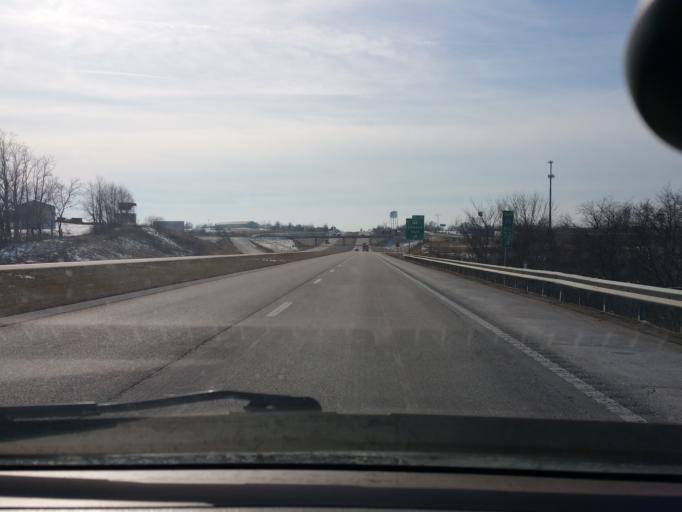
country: US
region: Missouri
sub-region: Clinton County
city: Lathrop
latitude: 39.4644
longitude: -94.3183
